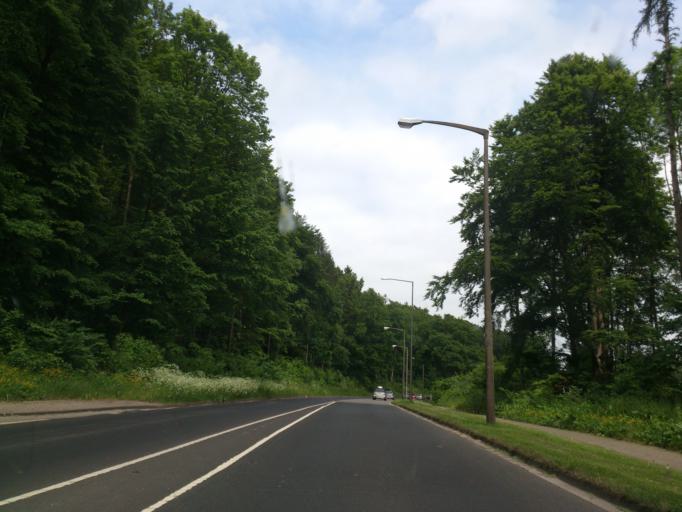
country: DE
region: Hesse
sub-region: Regierungsbezirk Kassel
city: Baunatal
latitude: 51.2970
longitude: 9.4119
